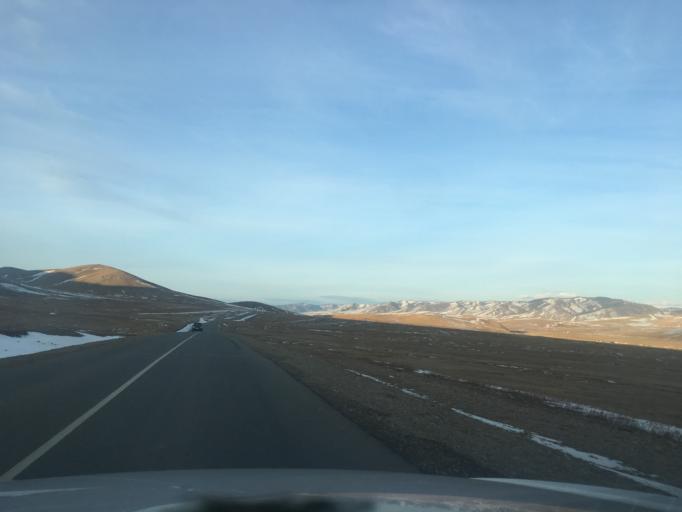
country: MN
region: Central Aimak
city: Mandal
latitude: 48.2235
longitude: 106.7144
